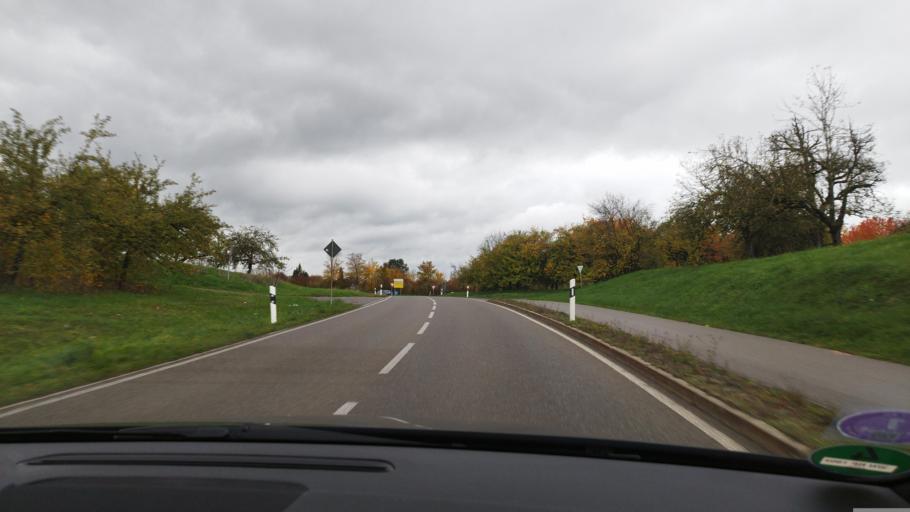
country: DE
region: Baden-Wuerttemberg
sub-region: Regierungsbezirk Stuttgart
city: Korb
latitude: 48.8538
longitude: 9.3555
